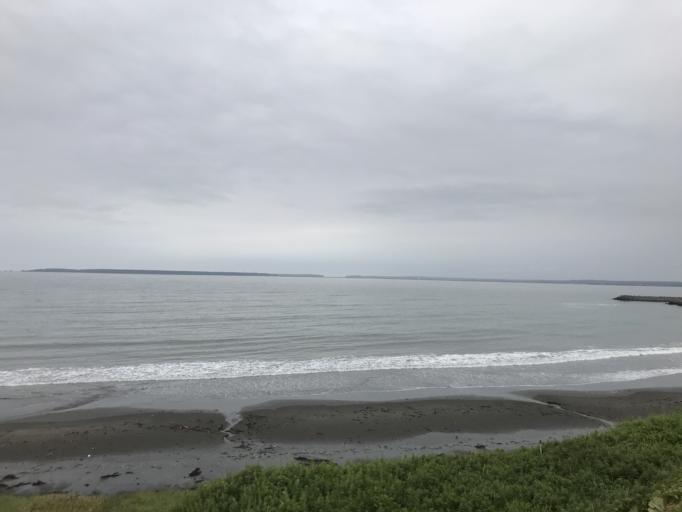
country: JP
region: Hokkaido
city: Nemuro
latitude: 43.1493
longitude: 145.1765
